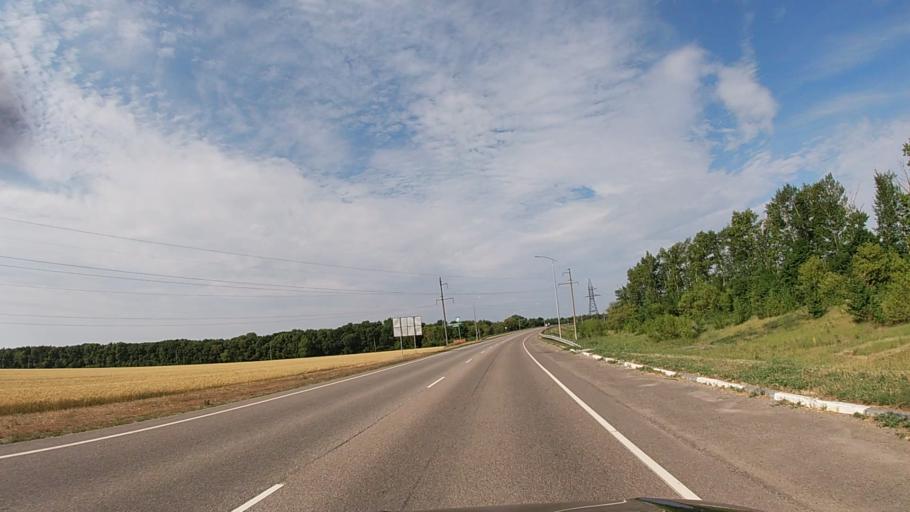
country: RU
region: Belgorod
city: Proletarskiy
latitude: 50.8055
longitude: 35.7416
